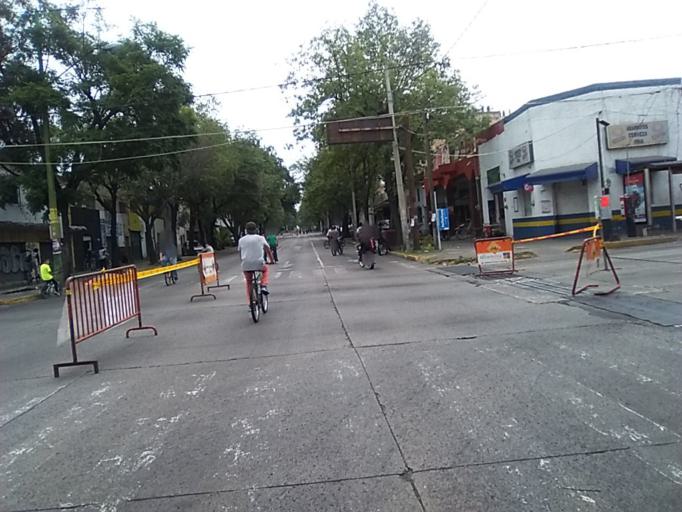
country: MX
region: Jalisco
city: Tlaquepaque
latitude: 20.6722
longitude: -103.3294
